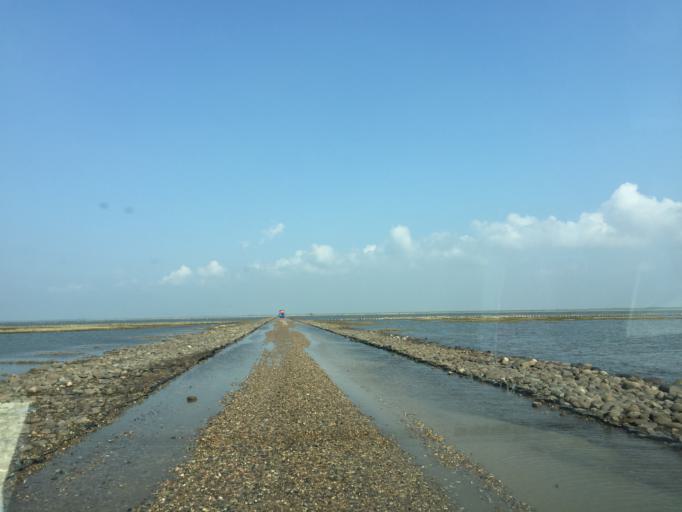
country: DK
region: South Denmark
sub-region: Esbjerg Kommune
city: Ribe
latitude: 55.3045
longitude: 8.6263
